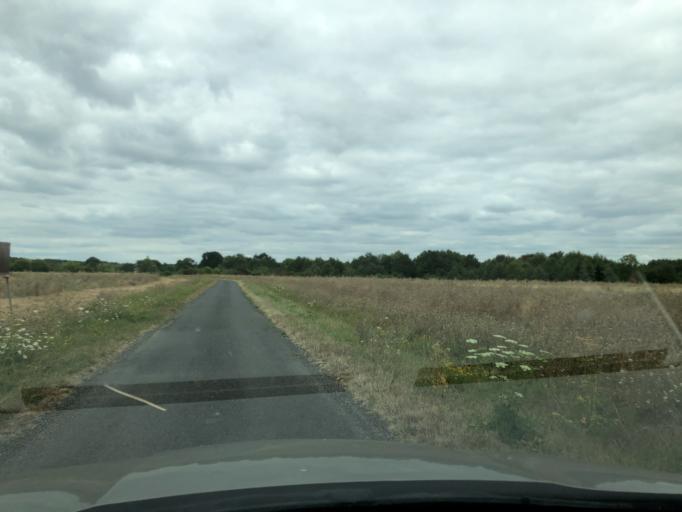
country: FR
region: Centre
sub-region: Departement d'Indre-et-Loire
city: Villandry
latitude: 47.3662
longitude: 0.4988
